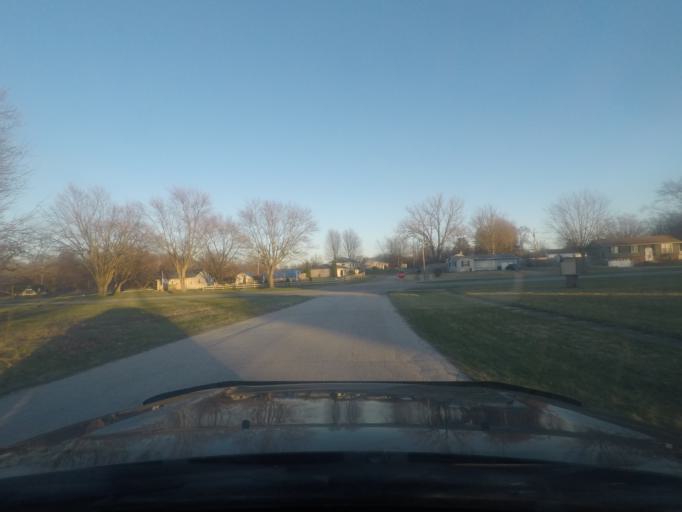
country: US
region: Indiana
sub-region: LaPorte County
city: Kingsford Heights
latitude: 41.4829
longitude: -86.6898
